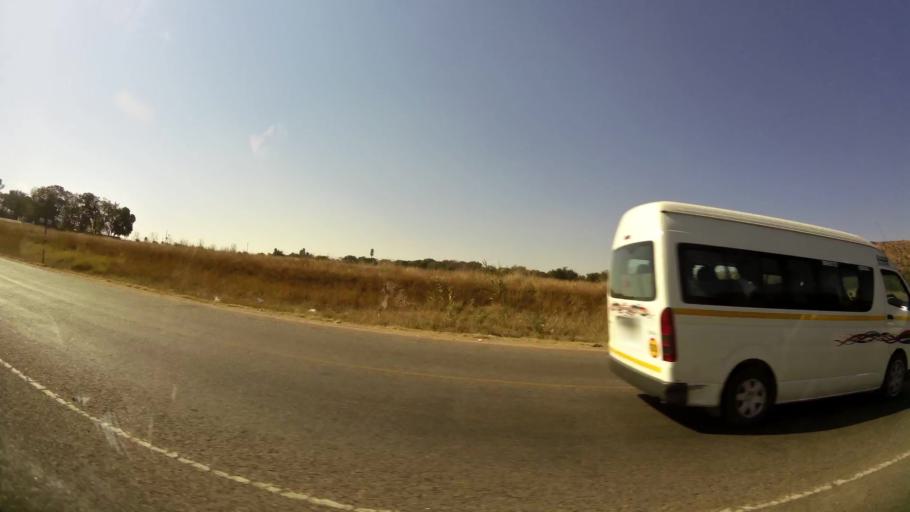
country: ZA
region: Gauteng
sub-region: City of Tshwane Metropolitan Municipality
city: Pretoria
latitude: -25.6881
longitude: 28.2932
